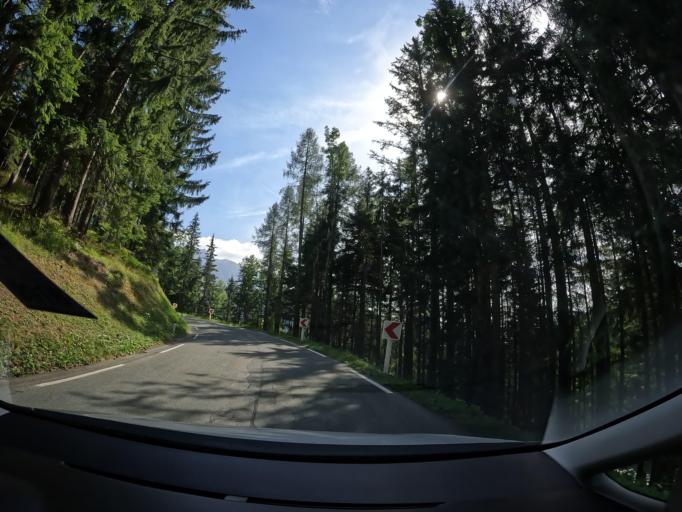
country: AT
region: Carinthia
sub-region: Politischer Bezirk Feldkirchen
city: Glanegg
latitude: 46.7435
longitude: 14.2227
